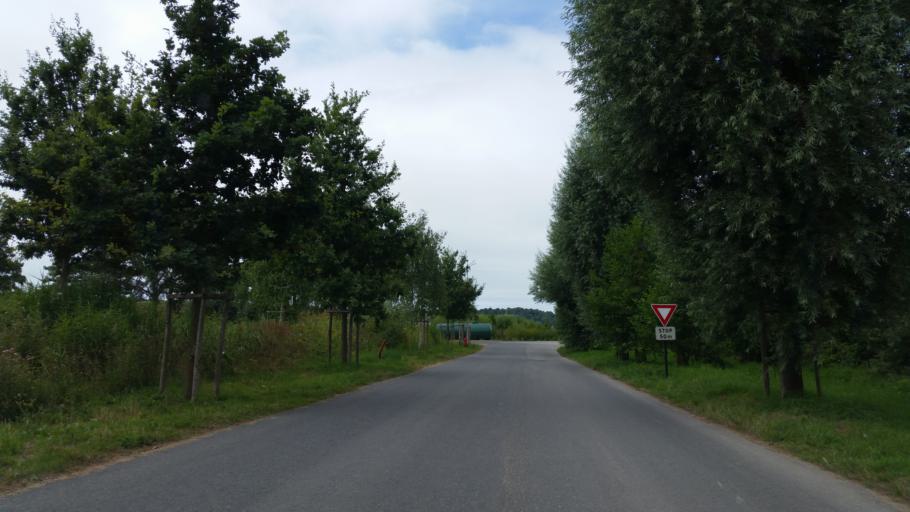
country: FR
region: Lower Normandy
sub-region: Departement du Calvados
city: La Riviere-Saint-Sauveur
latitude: 49.4200
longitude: 0.2612
